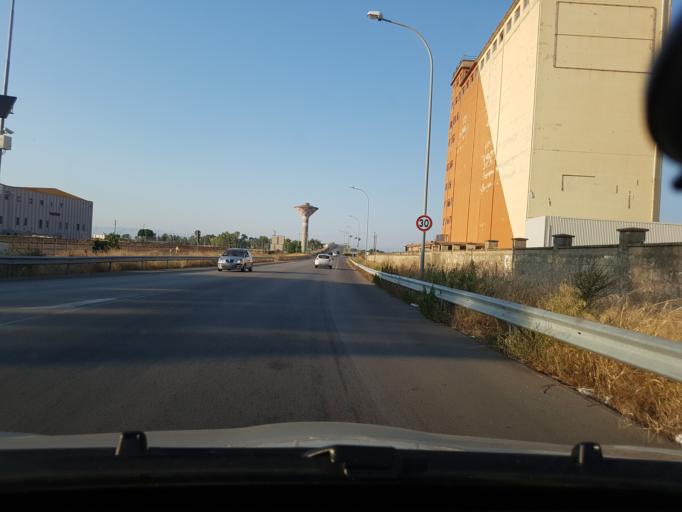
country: IT
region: Apulia
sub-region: Provincia di Foggia
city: Carapelle
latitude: 41.4026
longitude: 15.6502
